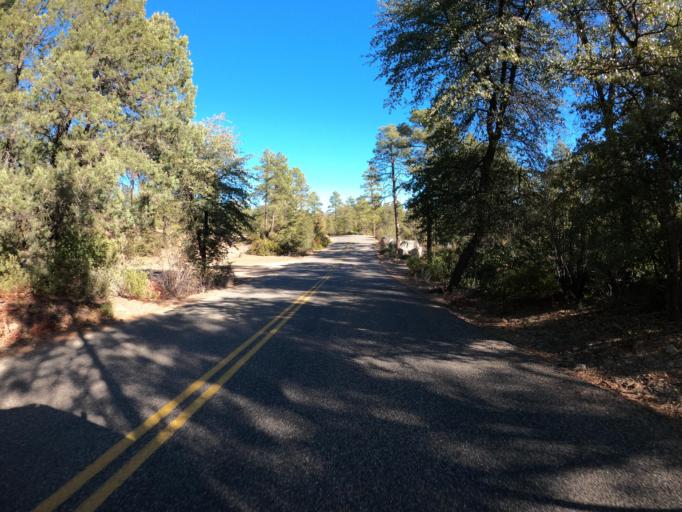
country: US
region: Arizona
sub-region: Yavapai County
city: Verde Village
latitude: 34.5805
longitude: -112.0633
